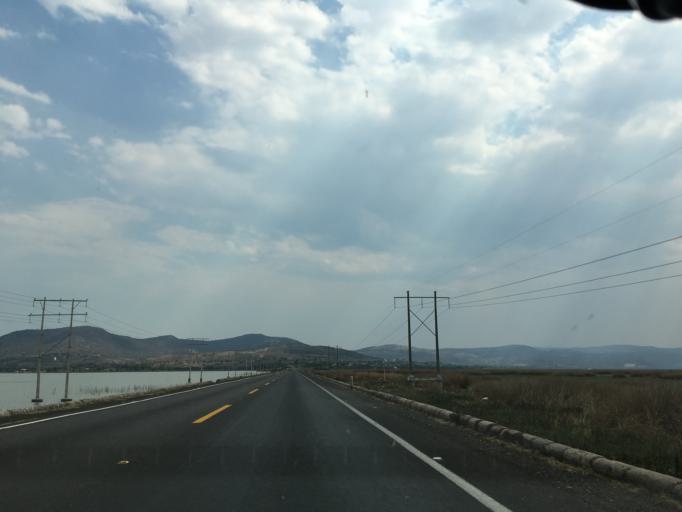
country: MX
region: Michoacan
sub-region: Cuitzeo
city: San Juan Benito Juarez (San Juan Tararameo)
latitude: 19.9398
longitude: -101.1382
